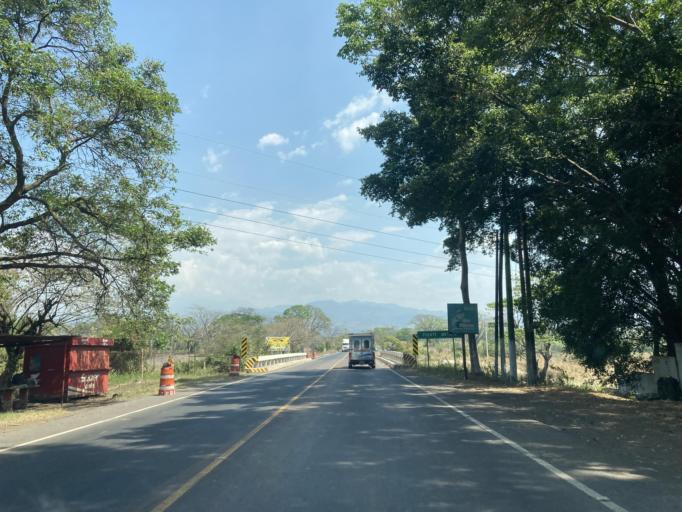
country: GT
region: Escuintla
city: Guanagazapa
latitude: 14.2025
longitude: -90.7089
